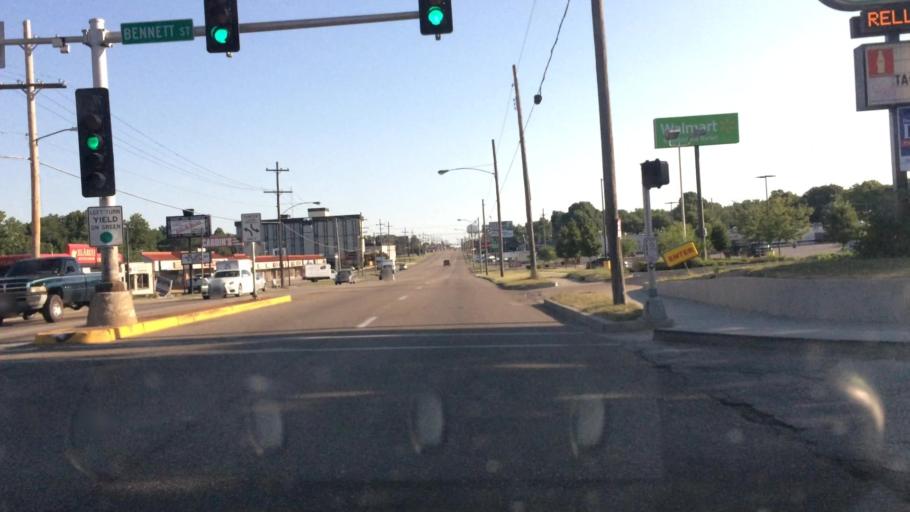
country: US
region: Missouri
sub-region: Greene County
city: Springfield
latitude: 37.1890
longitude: -93.2622
